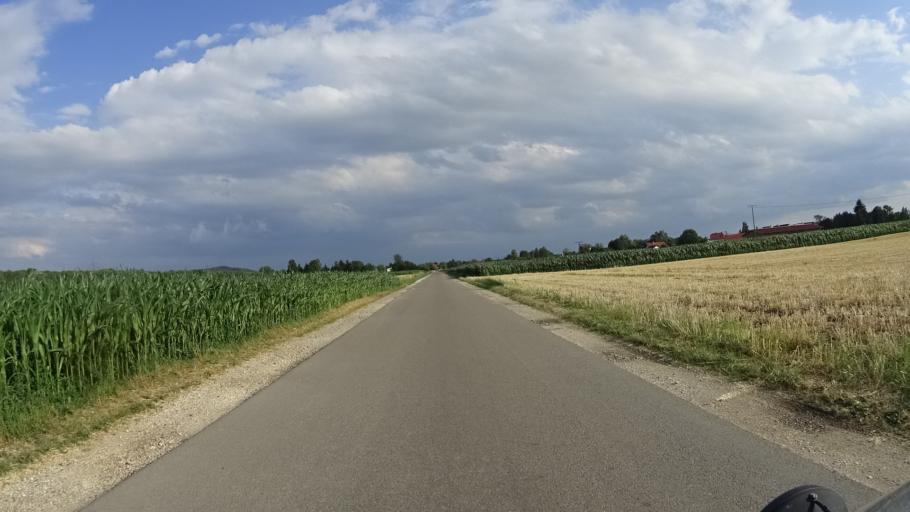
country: DE
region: Bavaria
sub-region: Swabia
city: Altenstadt
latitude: 48.1537
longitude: 10.0958
